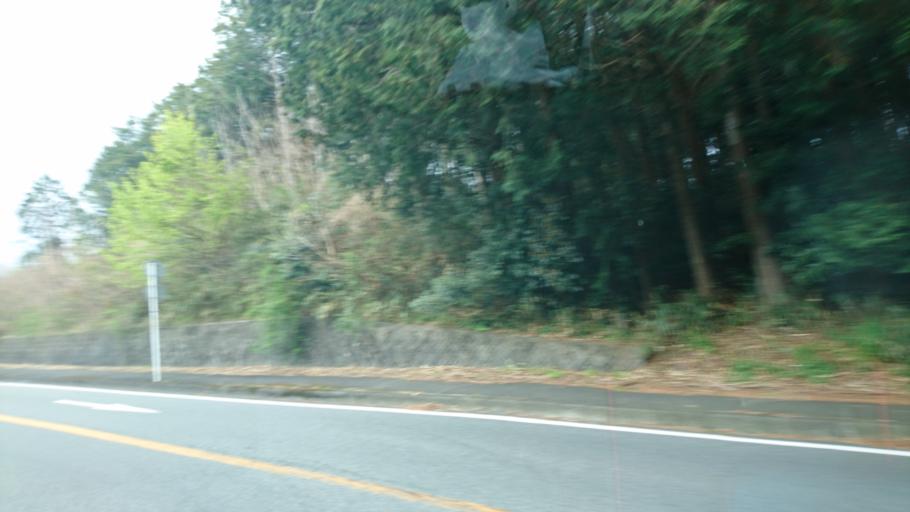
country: JP
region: Shizuoka
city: Fujinomiya
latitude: 35.2653
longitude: 138.6038
